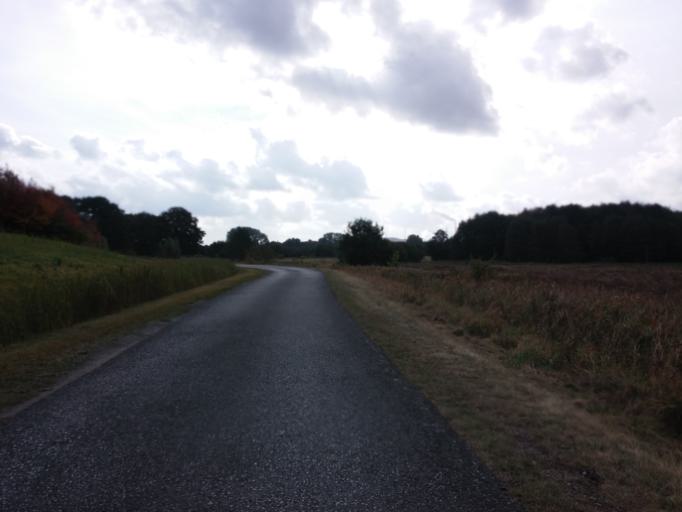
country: DE
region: North Rhine-Westphalia
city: Dorsten
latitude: 51.6500
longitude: 7.0181
